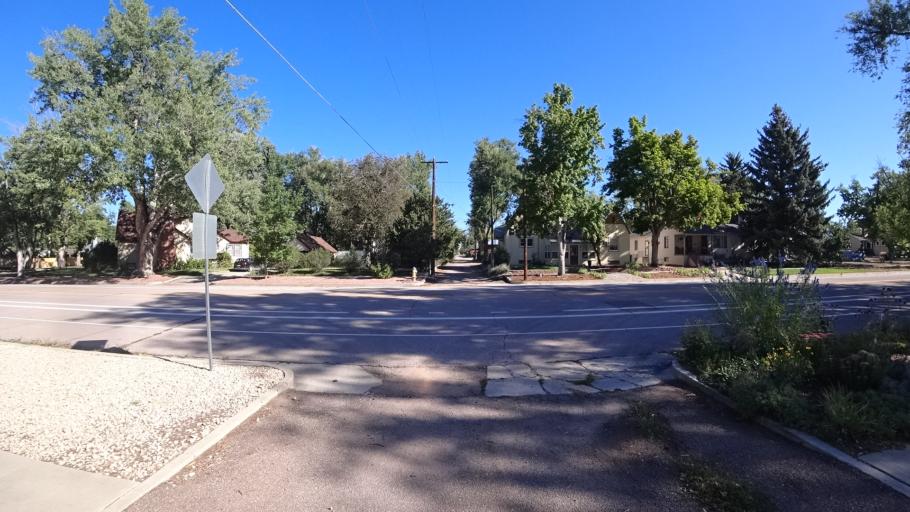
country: US
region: Colorado
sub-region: El Paso County
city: Colorado Springs
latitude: 38.8415
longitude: -104.8011
